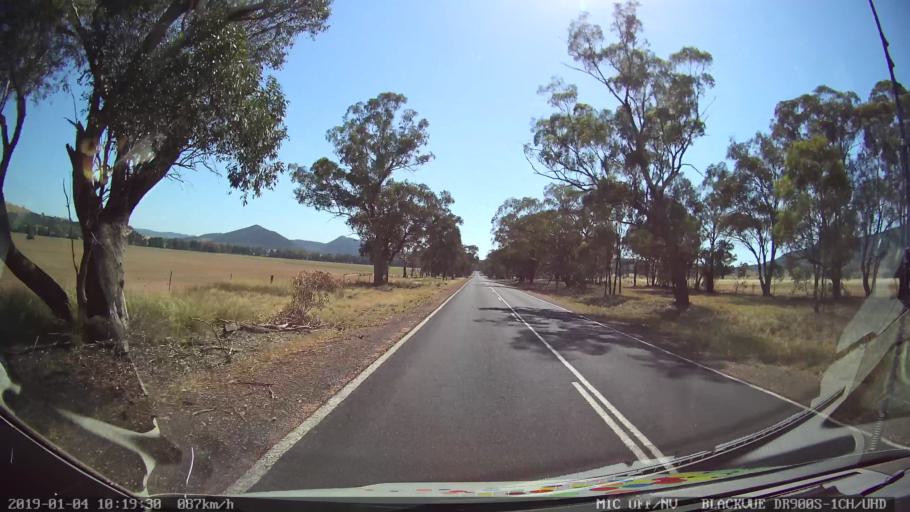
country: AU
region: New South Wales
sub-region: Cabonne
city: Canowindra
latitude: -33.3764
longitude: 148.4816
